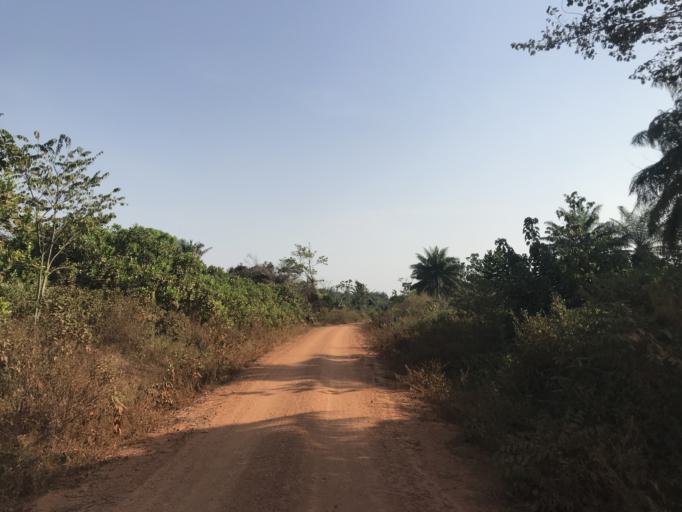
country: NG
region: Osun
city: Inisa
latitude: 7.7928
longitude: 4.2959
